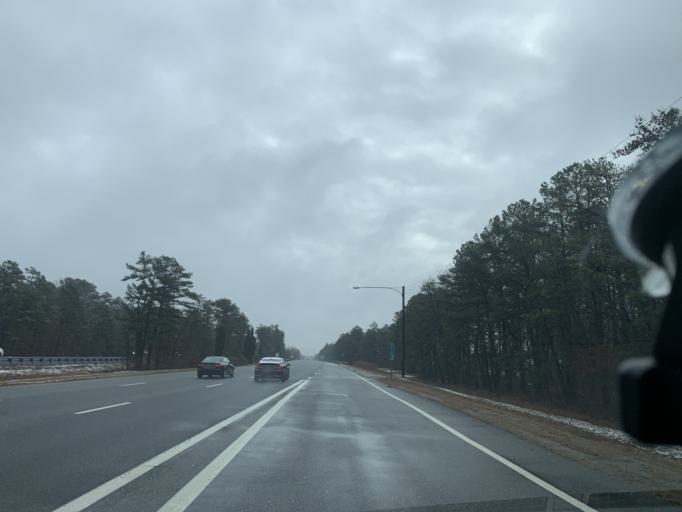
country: US
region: New Jersey
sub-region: Atlantic County
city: Pomona
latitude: 39.4445
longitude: -74.6158
